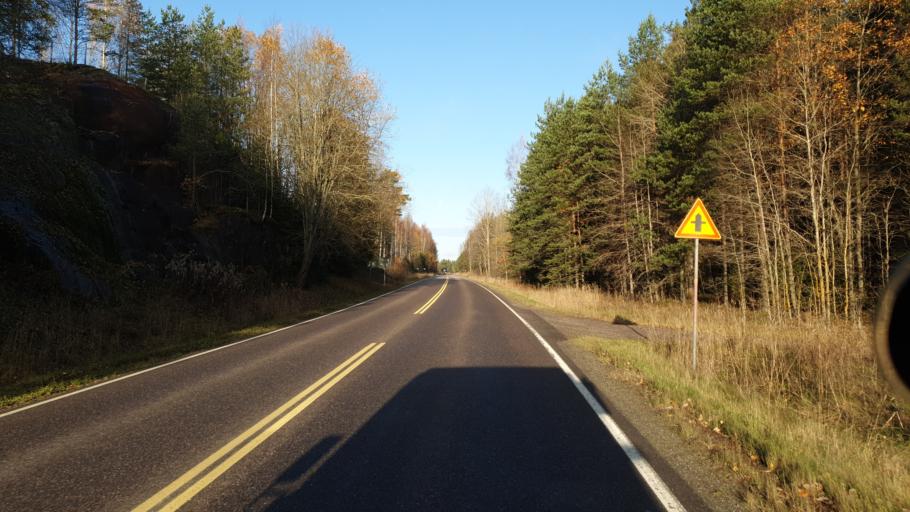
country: FI
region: Uusimaa
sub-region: Helsinki
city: Siuntio
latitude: 60.1922
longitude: 24.2004
